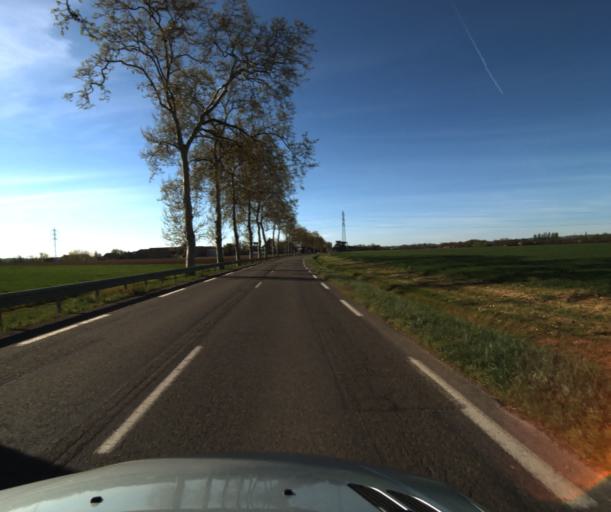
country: FR
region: Midi-Pyrenees
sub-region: Departement du Tarn-et-Garonne
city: Montbeton
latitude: 44.0400
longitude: 1.3060
